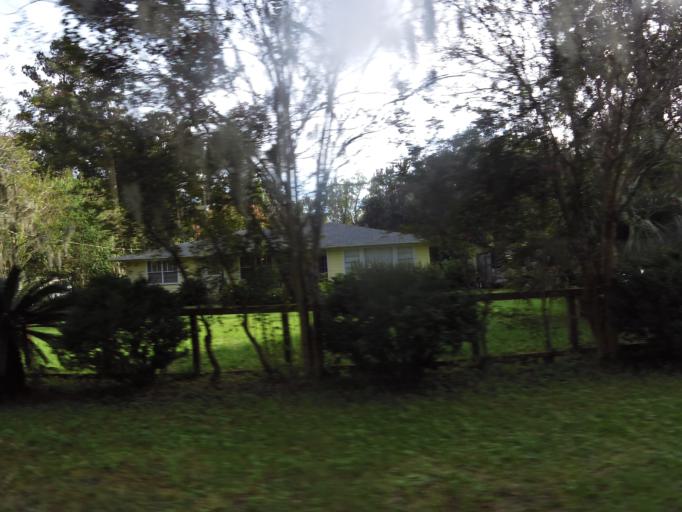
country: US
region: Florida
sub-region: Duval County
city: Jacksonville
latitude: 30.4186
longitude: -81.6543
